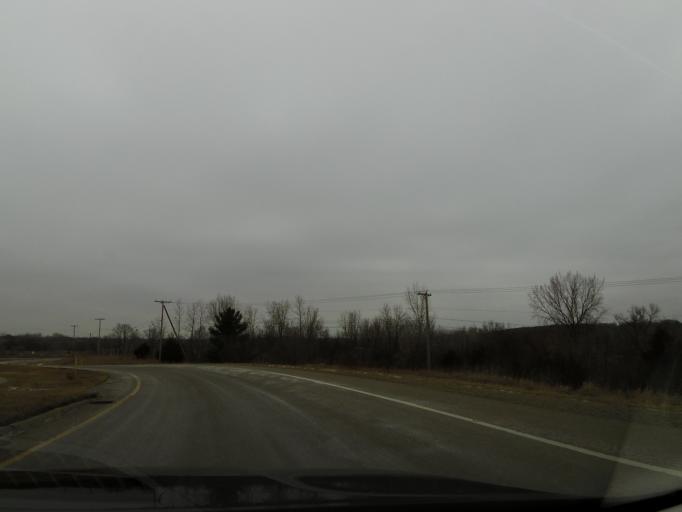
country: US
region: Minnesota
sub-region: Hennepin County
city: Orono
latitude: 44.9938
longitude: -93.6172
